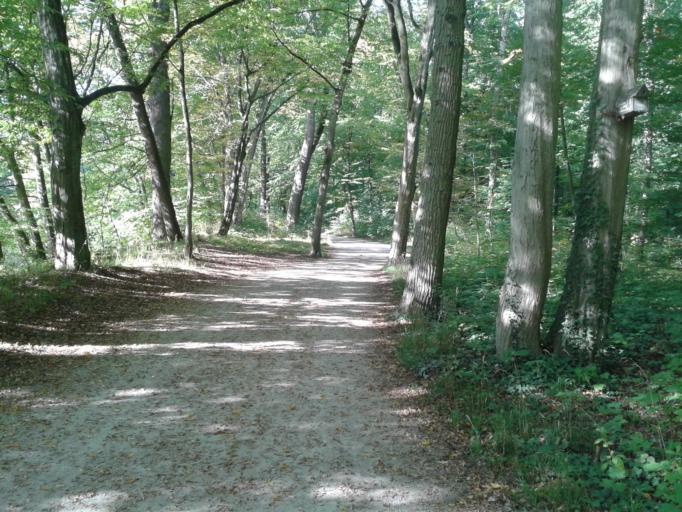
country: DE
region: Bavaria
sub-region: Upper Franconia
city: Bamberg
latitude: 49.8754
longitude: 10.9018
